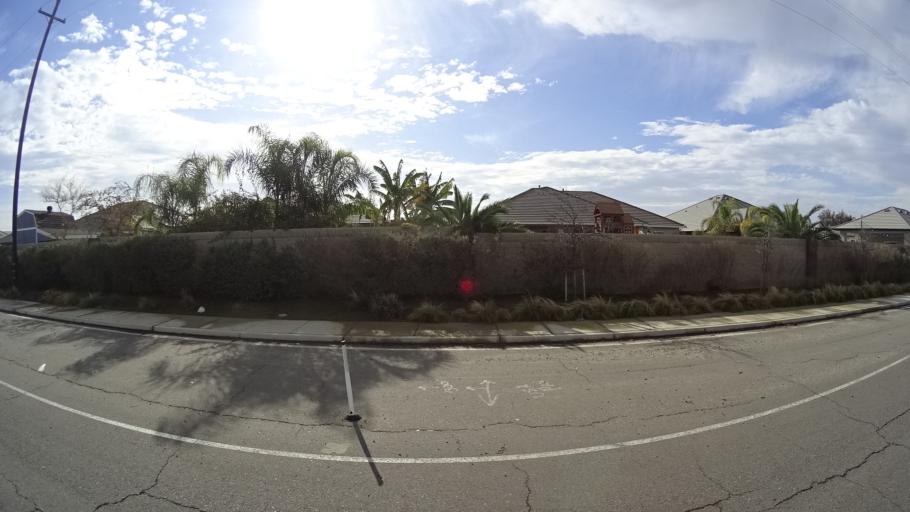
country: US
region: California
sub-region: Kern County
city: Greenacres
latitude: 35.4270
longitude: -119.0999
